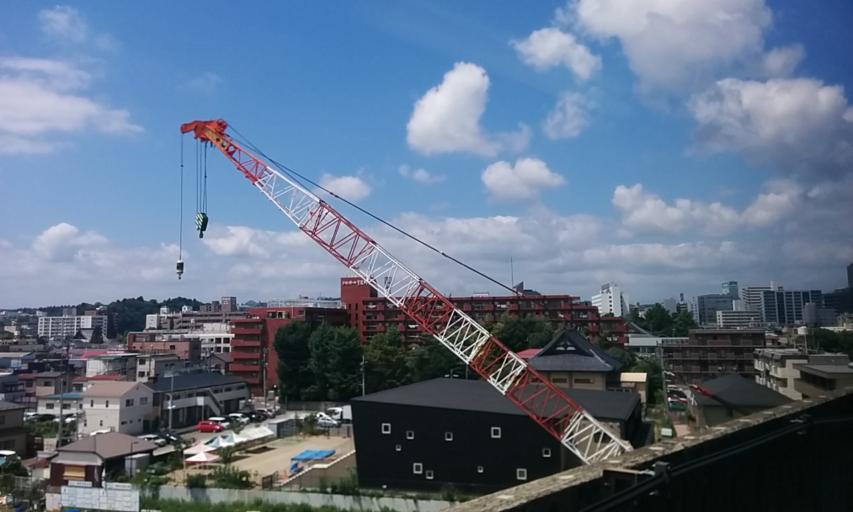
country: JP
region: Miyagi
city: Sendai
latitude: 38.2492
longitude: 140.8898
